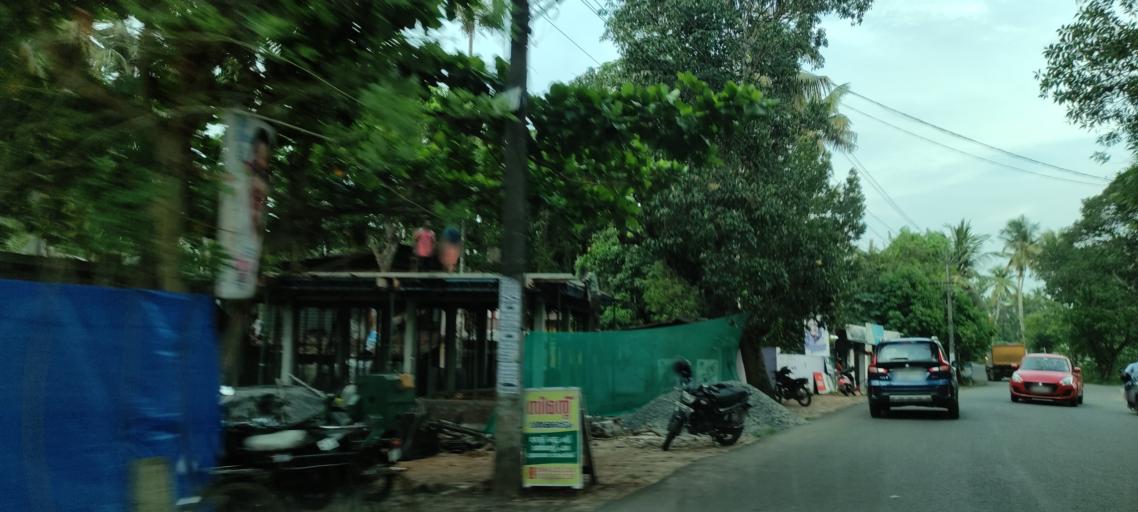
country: IN
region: Kerala
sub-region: Kottayam
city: Vaikam
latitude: 9.7276
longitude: 76.3615
